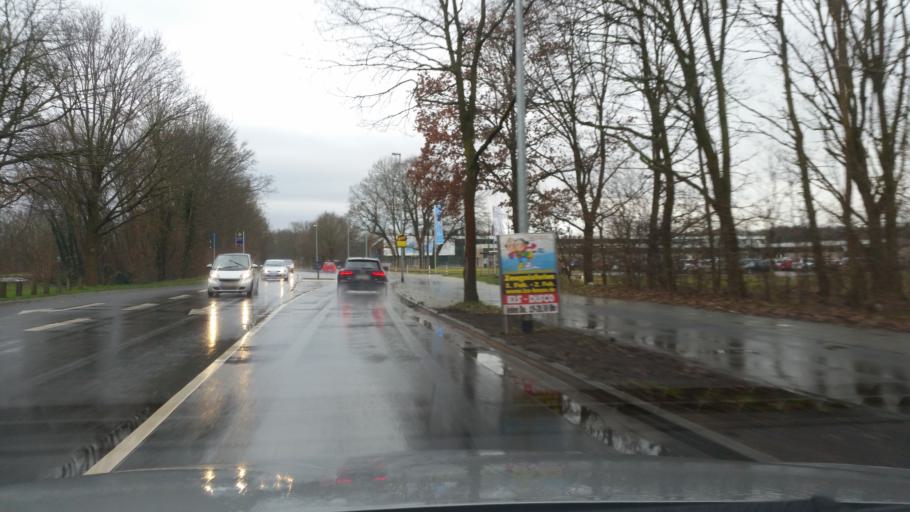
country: DE
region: Lower Saxony
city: Langenhagen
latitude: 52.4483
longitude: 9.7556
